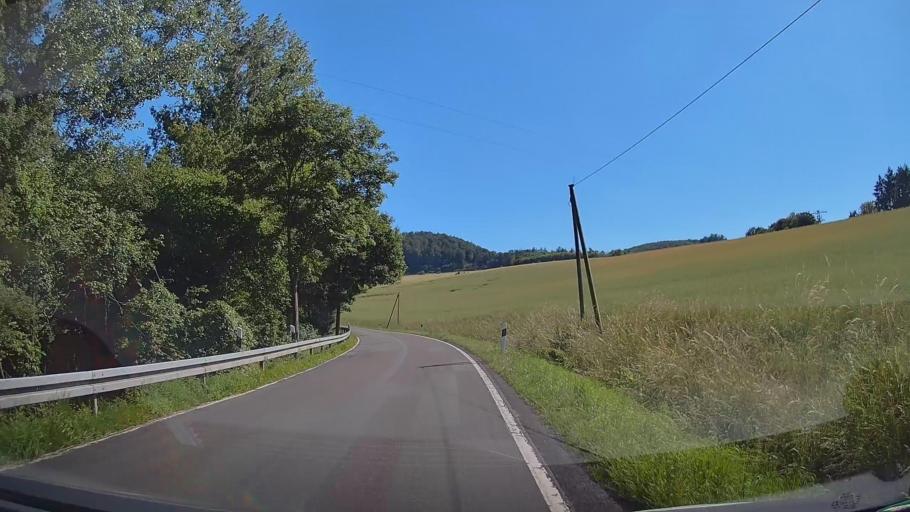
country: DE
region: Lower Saxony
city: Vahlbruch
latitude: 51.9921
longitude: 9.3383
